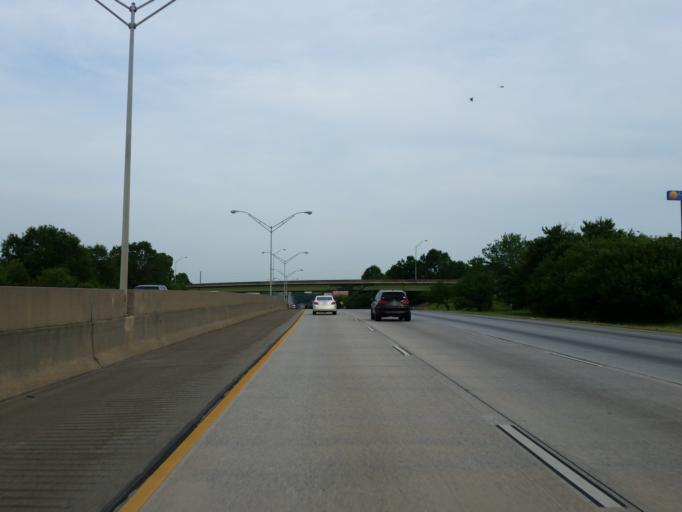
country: US
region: Georgia
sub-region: Monroe County
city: Forsyth
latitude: 33.0292
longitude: -83.9122
